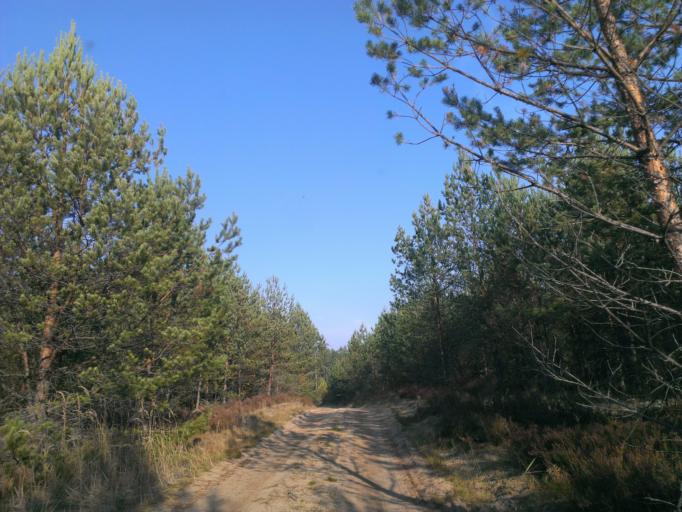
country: LV
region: Garkalne
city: Garkalne
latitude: 57.0231
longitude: 24.4883
